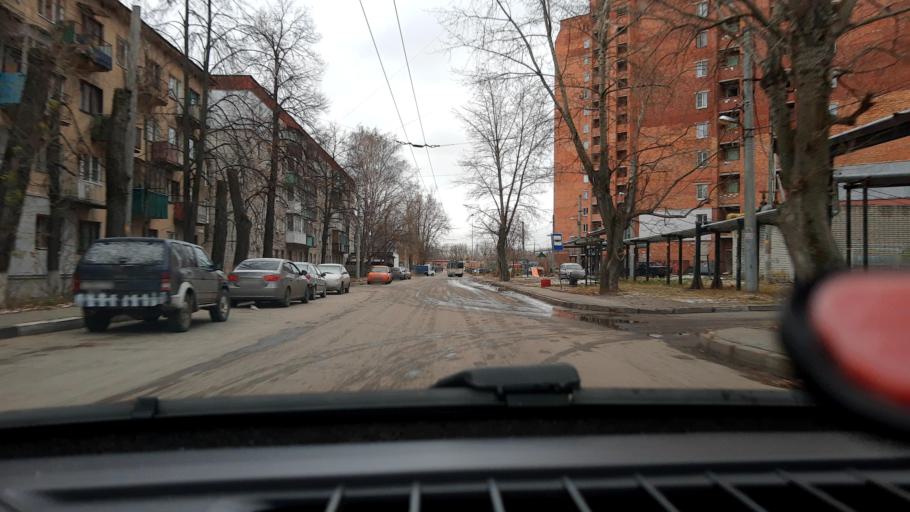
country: RU
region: Nizjnij Novgorod
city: Gorbatovka
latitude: 56.2866
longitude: 43.8466
